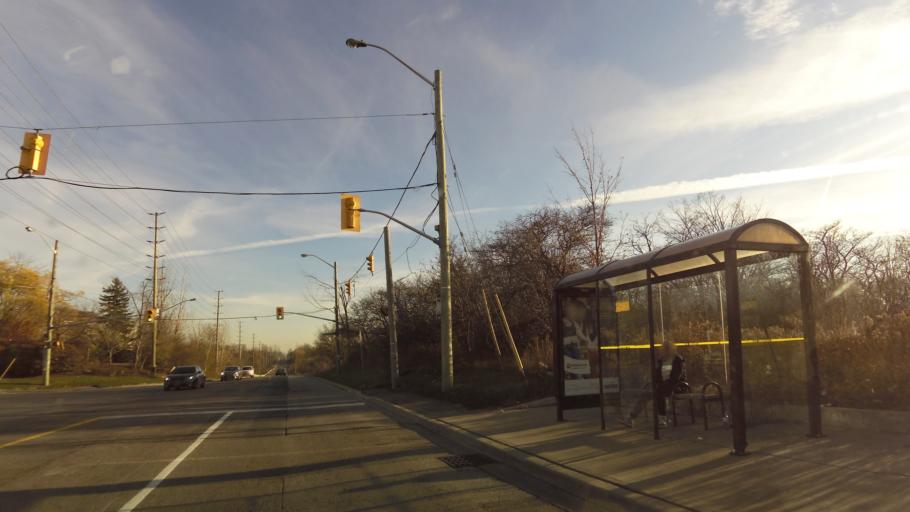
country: CA
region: Ontario
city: Brampton
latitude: 43.7702
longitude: -79.7075
